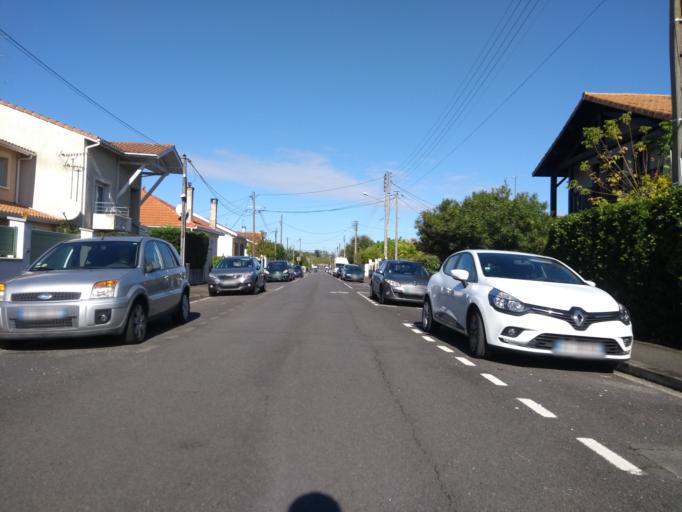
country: FR
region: Aquitaine
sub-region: Departement de la Gironde
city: Talence
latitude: 44.8045
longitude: -0.6121
